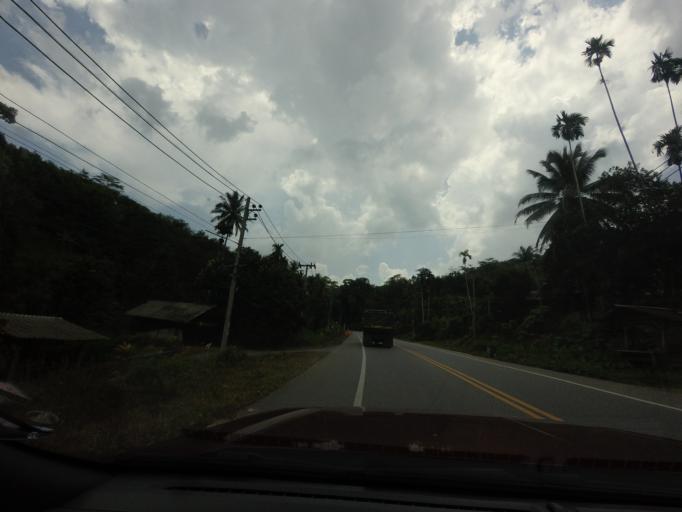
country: TH
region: Yala
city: Than To
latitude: 6.0805
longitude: 101.1864
